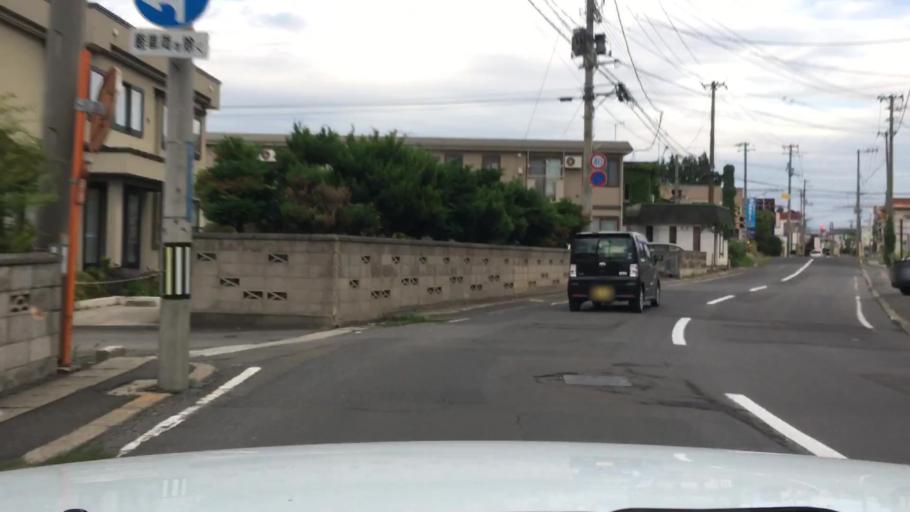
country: JP
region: Aomori
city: Hirosaki
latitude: 40.5858
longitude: 140.4693
